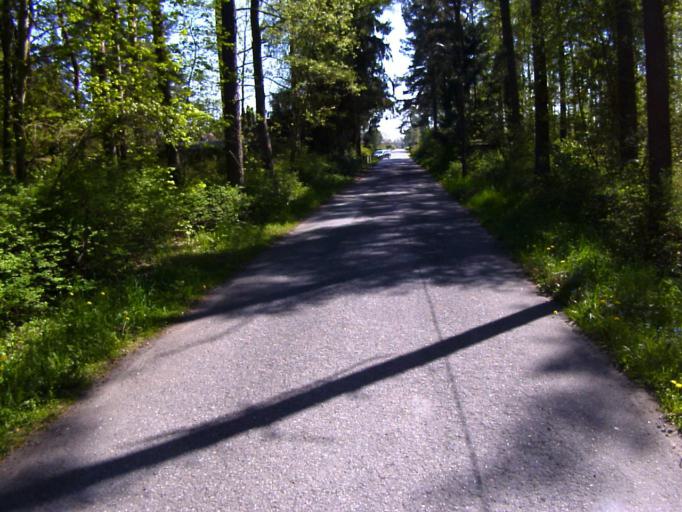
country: SE
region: Skane
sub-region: Kristianstads Kommun
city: Degeberga
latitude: 55.9032
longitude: 14.0923
